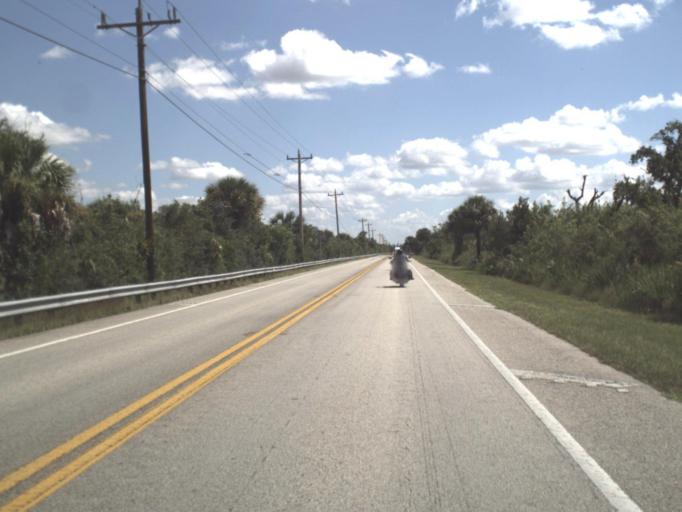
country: US
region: Florida
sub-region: Collier County
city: Marco
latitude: 25.9511
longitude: -81.4830
